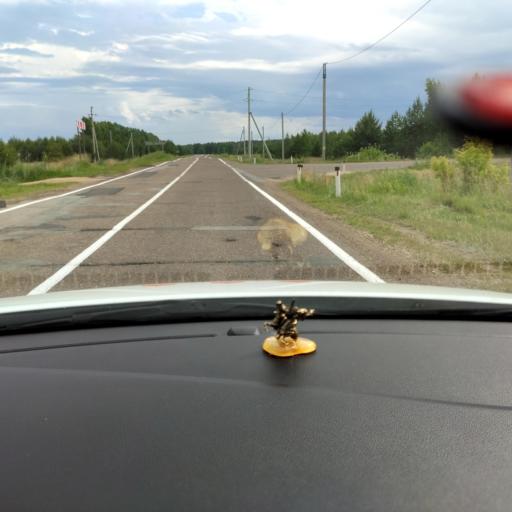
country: RU
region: Tatarstan
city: Kuybyshevskiy Zaton
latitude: 55.3529
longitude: 49.2927
